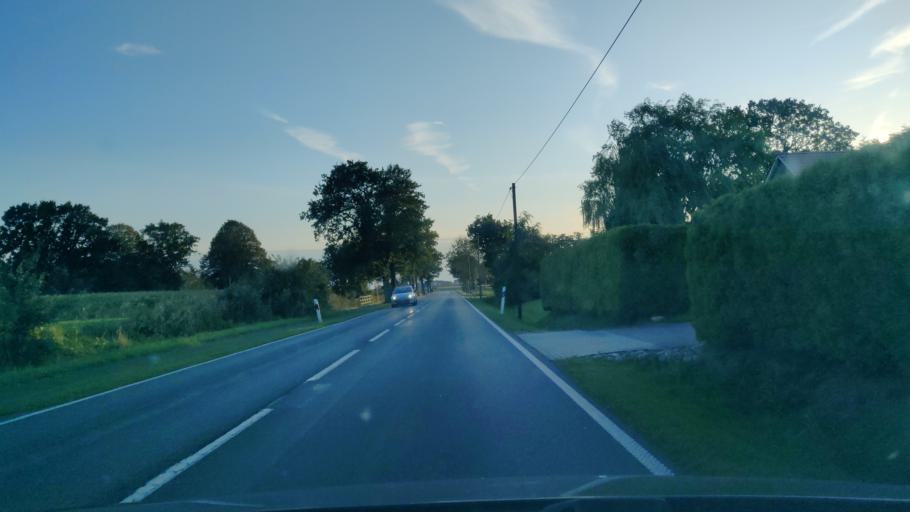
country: DE
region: Lower Saxony
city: Aurich
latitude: 53.4385
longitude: 7.3938
